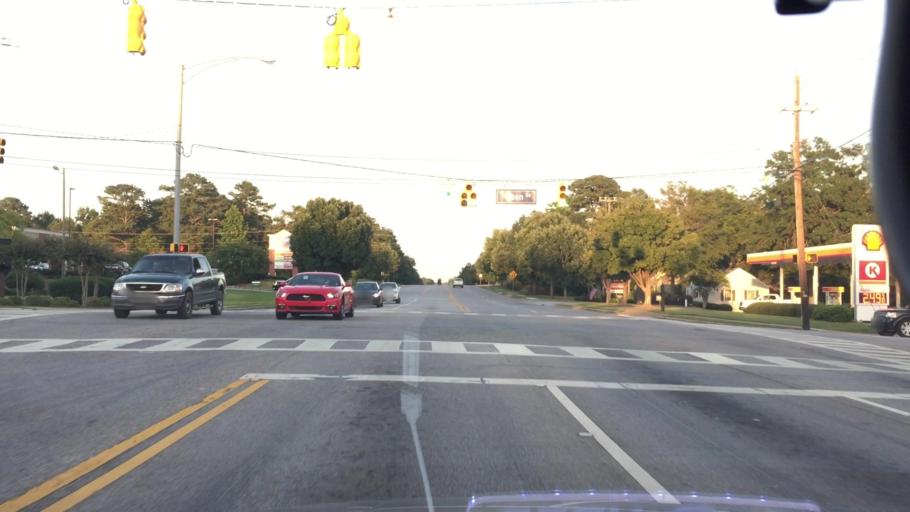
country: US
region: Alabama
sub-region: Lee County
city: Auburn
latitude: 32.6090
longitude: -85.4651
